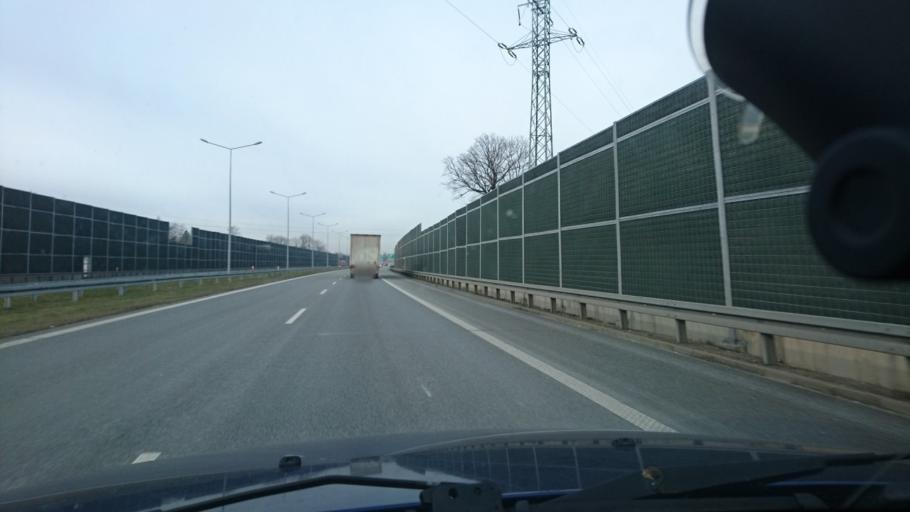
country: PL
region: Silesian Voivodeship
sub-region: Powiat bielski
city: Wilkowice
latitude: 49.7772
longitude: 19.0755
